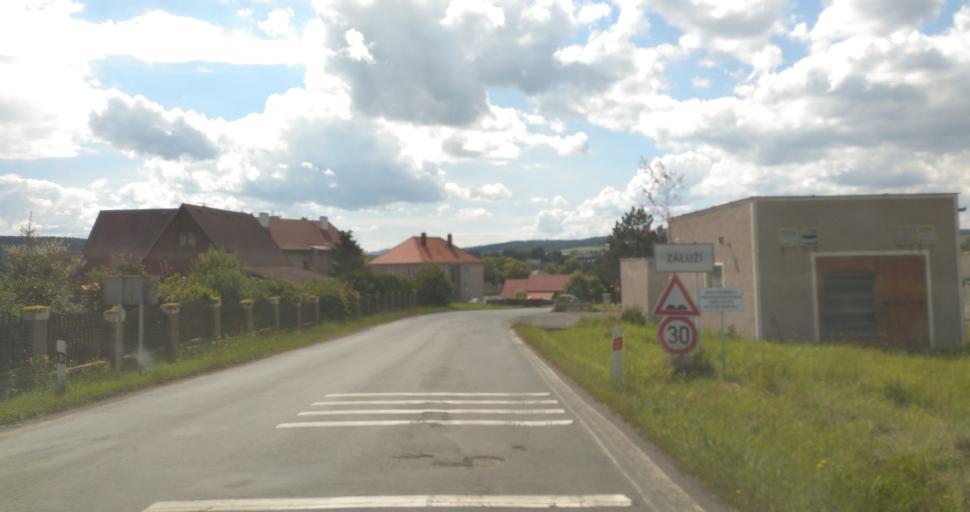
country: CZ
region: Central Bohemia
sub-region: Okres Beroun
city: Horovice
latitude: 49.8470
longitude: 13.8649
